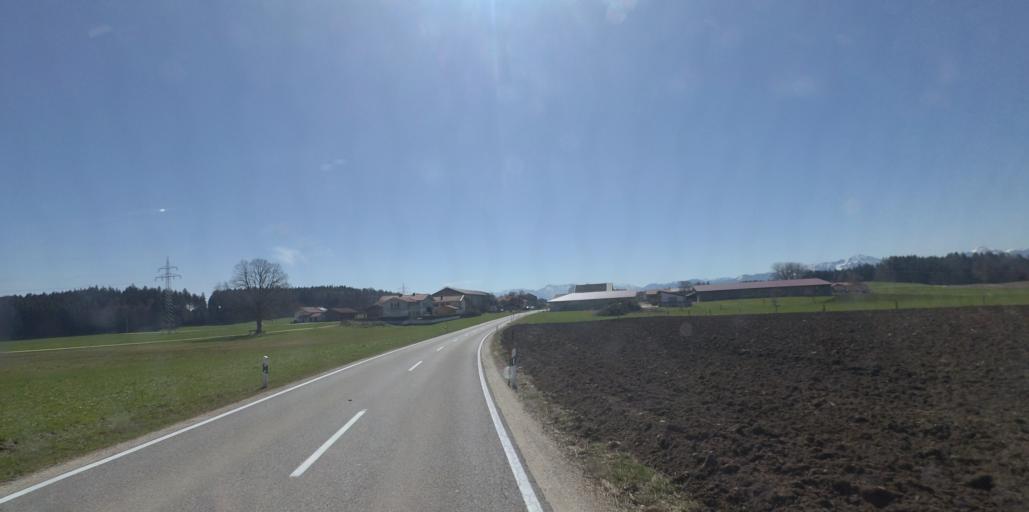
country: DE
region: Bavaria
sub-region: Upper Bavaria
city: Nussdorf
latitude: 47.8994
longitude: 12.6037
